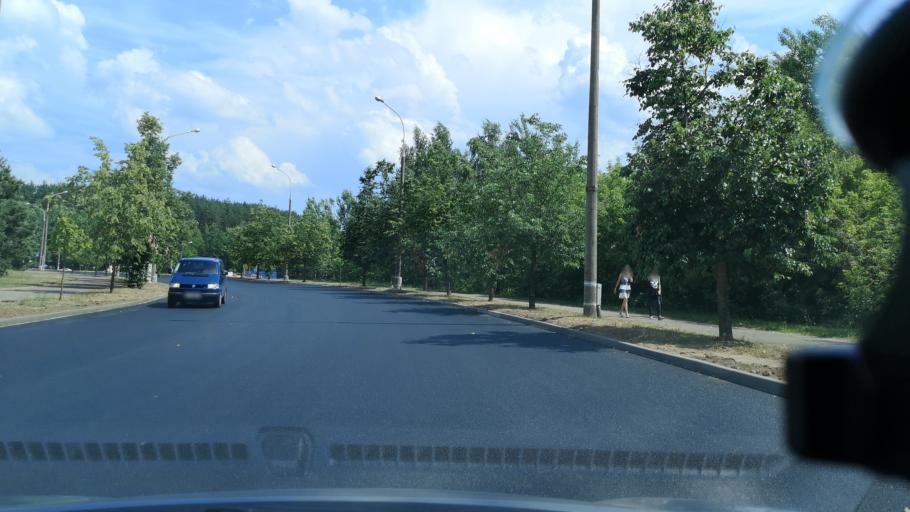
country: BY
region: Minsk
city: Lyeskawka
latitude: 53.9328
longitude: 27.6957
